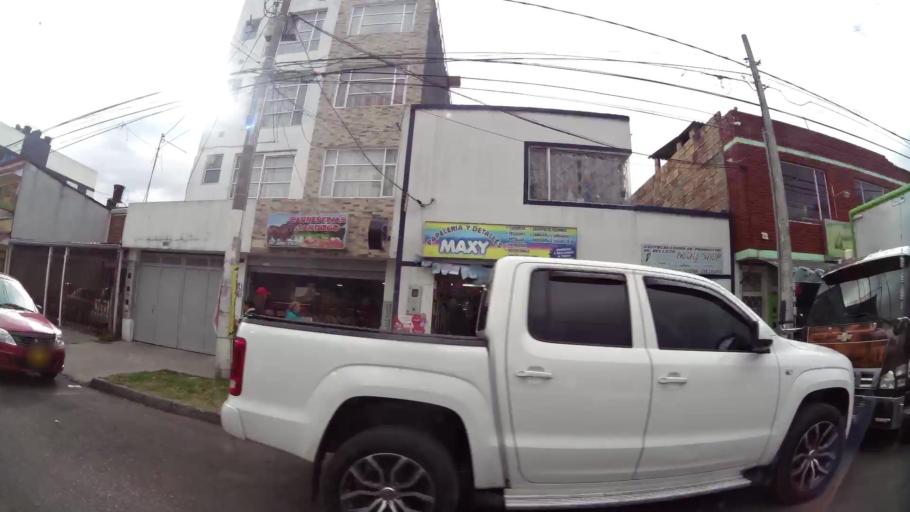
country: CO
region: Bogota D.C.
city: Bogota
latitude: 4.6092
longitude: -74.1129
